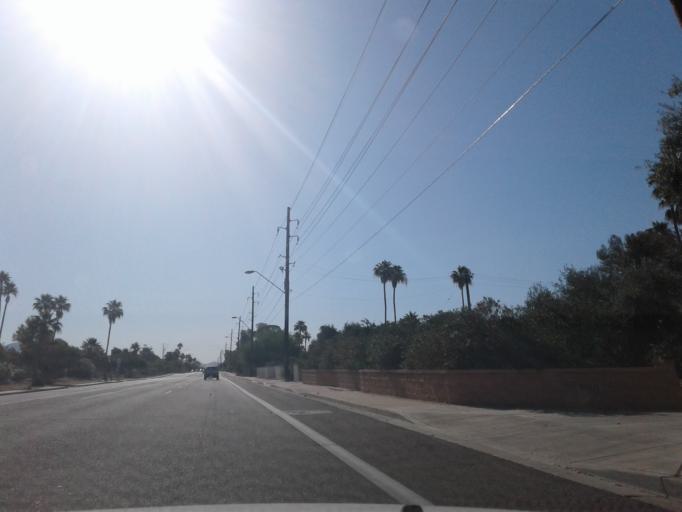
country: US
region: Arizona
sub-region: Maricopa County
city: Paradise Valley
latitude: 33.5970
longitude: -111.9549
